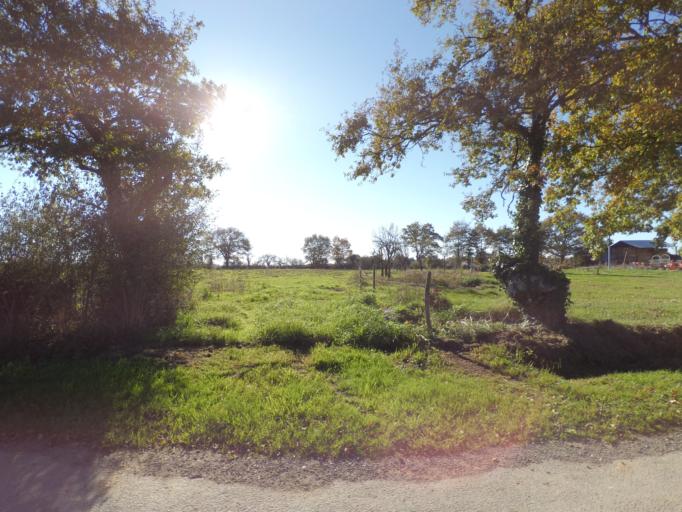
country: FR
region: Pays de la Loire
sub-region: Departement de la Vendee
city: Saint-Hilaire-de-Loulay
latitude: 46.9980
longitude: -1.3752
